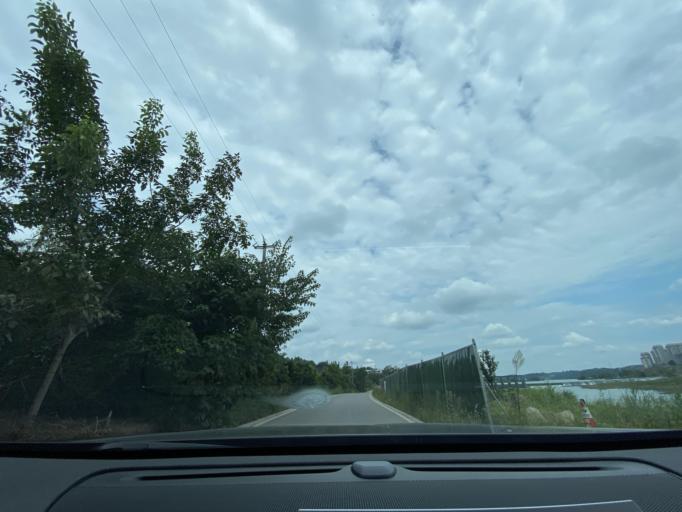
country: CN
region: Sichuan
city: Jiancheng
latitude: 30.4363
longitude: 104.5289
